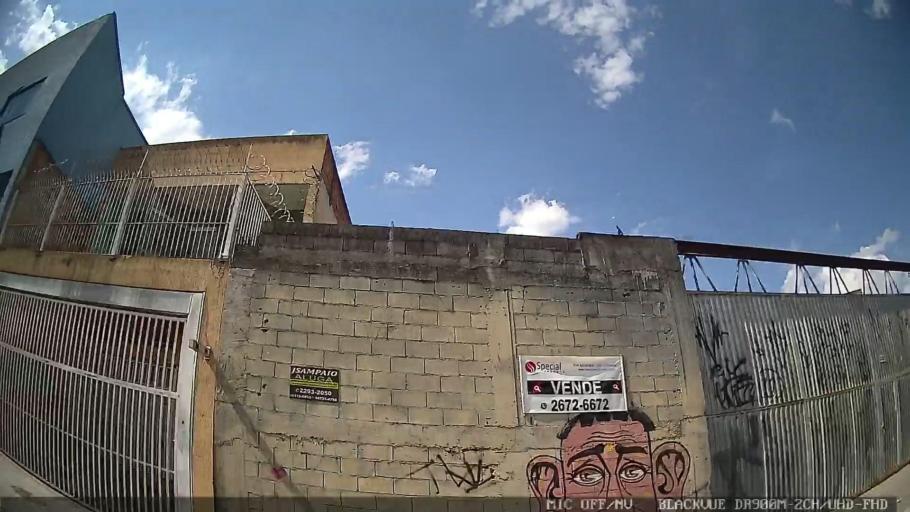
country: BR
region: Sao Paulo
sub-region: Guarulhos
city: Guarulhos
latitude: -23.5203
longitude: -46.5078
